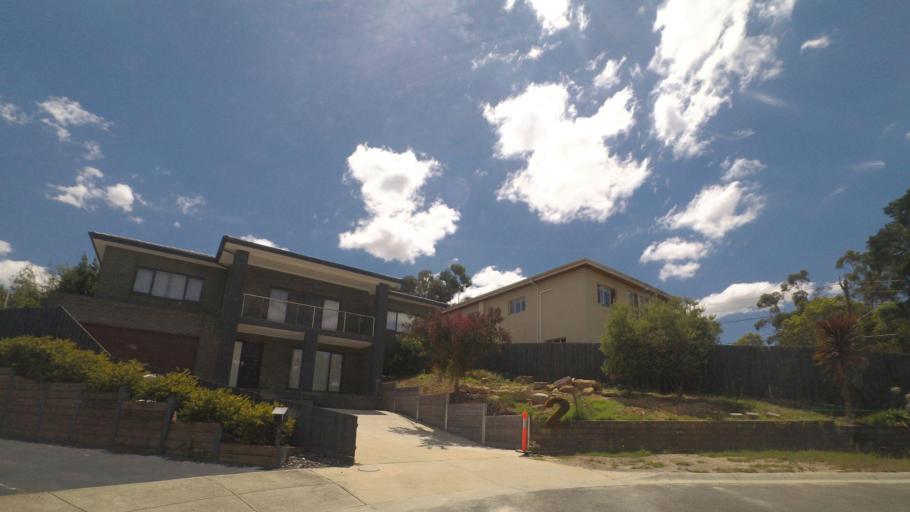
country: AU
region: Victoria
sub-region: Maroondah
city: Croydon Hills
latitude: -37.7626
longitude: 145.2817
